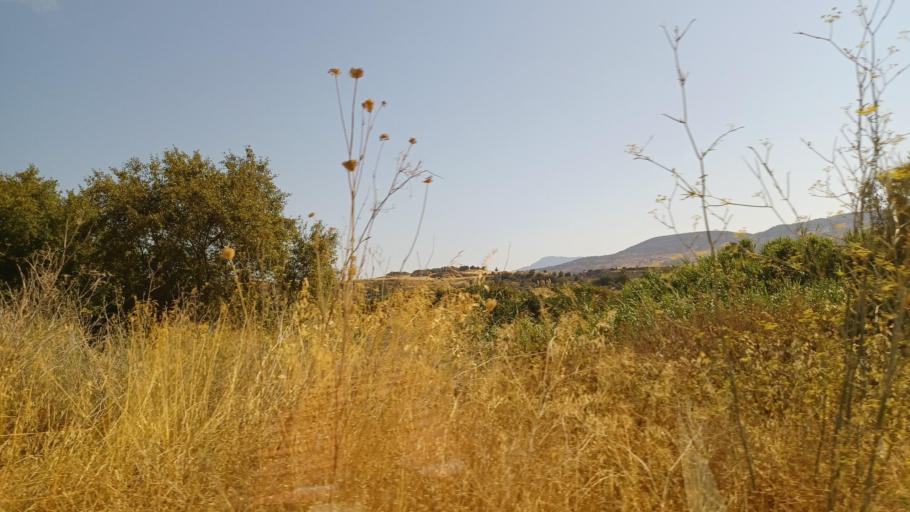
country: CY
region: Pafos
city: Polis
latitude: 35.0035
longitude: 32.4325
